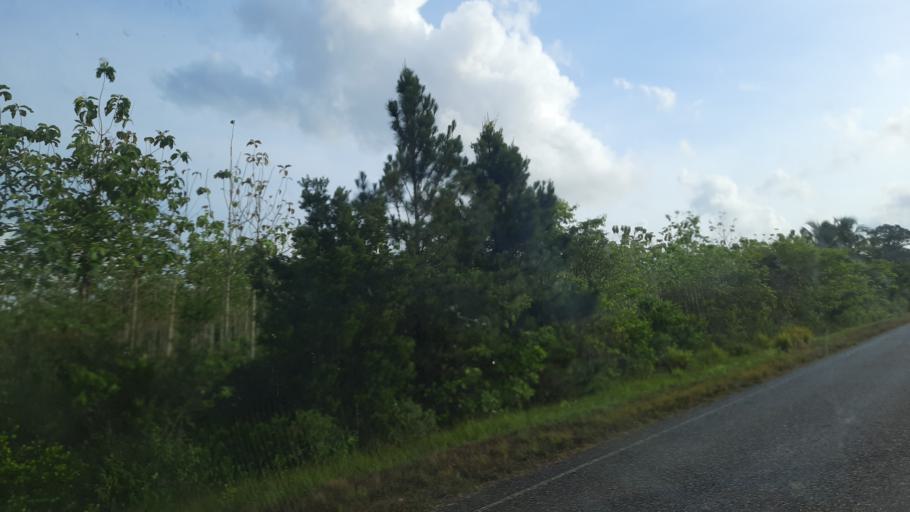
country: BZ
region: Stann Creek
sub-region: Dangriga
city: Dangriga
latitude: 16.9405
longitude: -88.3326
